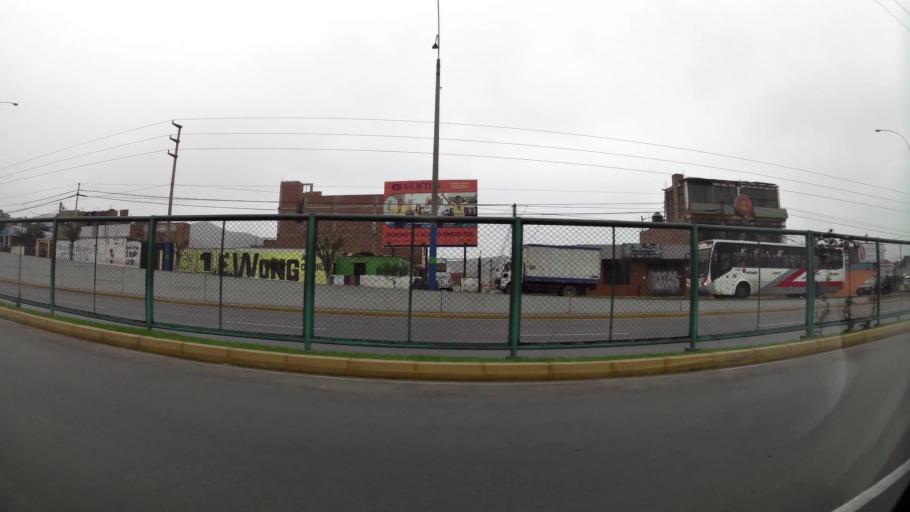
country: PE
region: Lima
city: Ventanilla
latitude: -11.8848
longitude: -77.1261
